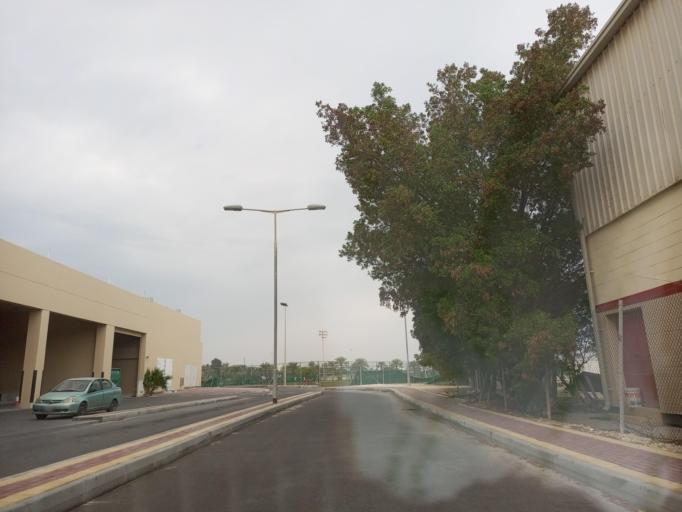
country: BH
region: Muharraq
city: Al Muharraq
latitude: 26.2555
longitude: 50.6262
